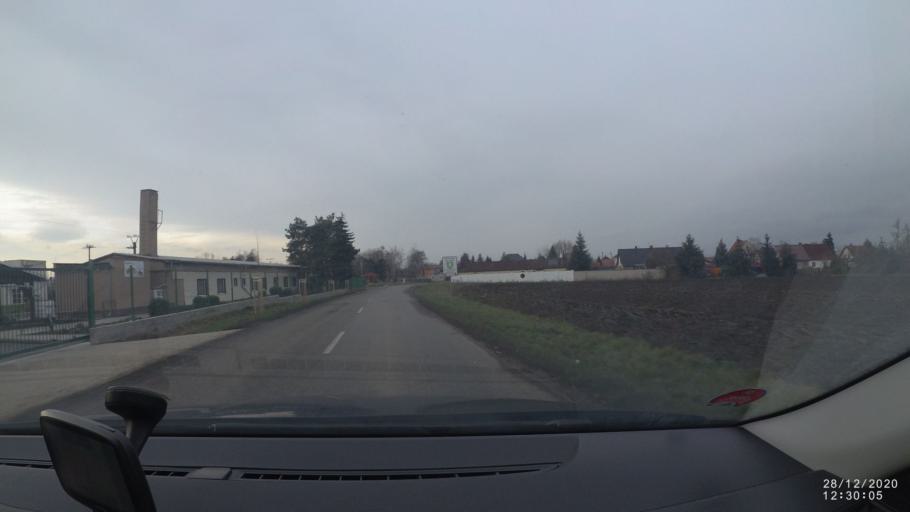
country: CZ
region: Central Bohemia
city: Kostelec nad Labem
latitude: 50.1997
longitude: 14.6020
